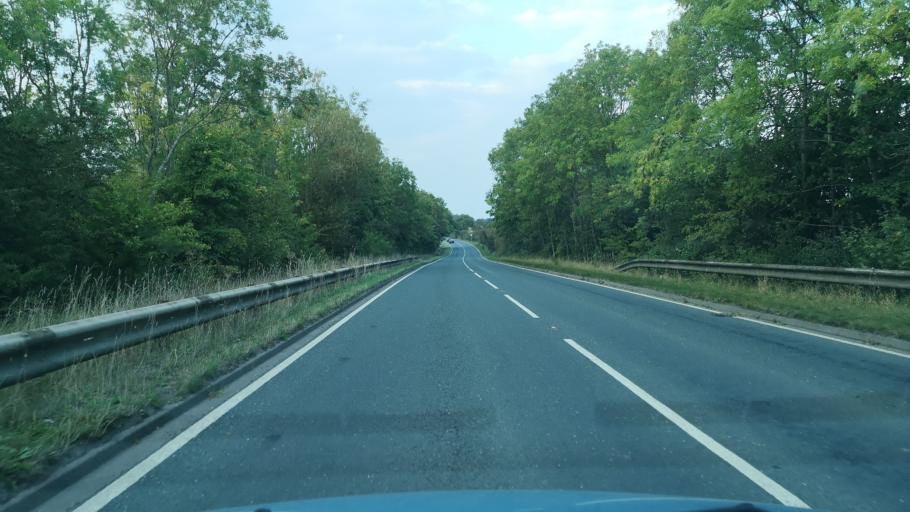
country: GB
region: England
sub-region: East Riding of Yorkshire
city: Rawcliffe
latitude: 53.6812
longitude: -0.9876
